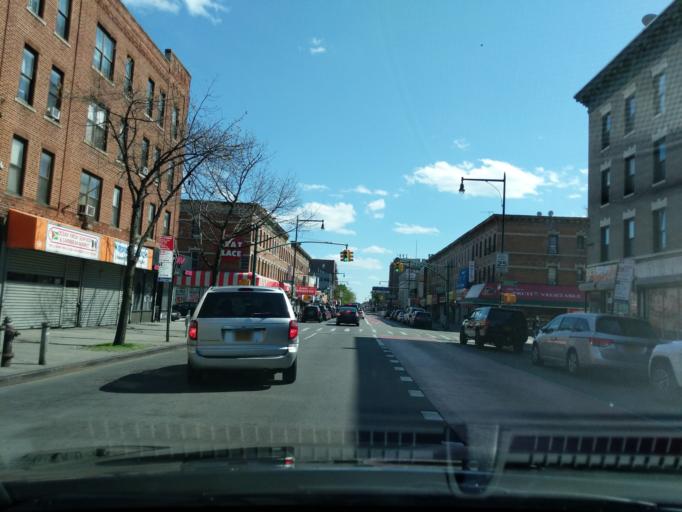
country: US
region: New York
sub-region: Kings County
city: Brooklyn
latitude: 40.6521
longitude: -73.9497
